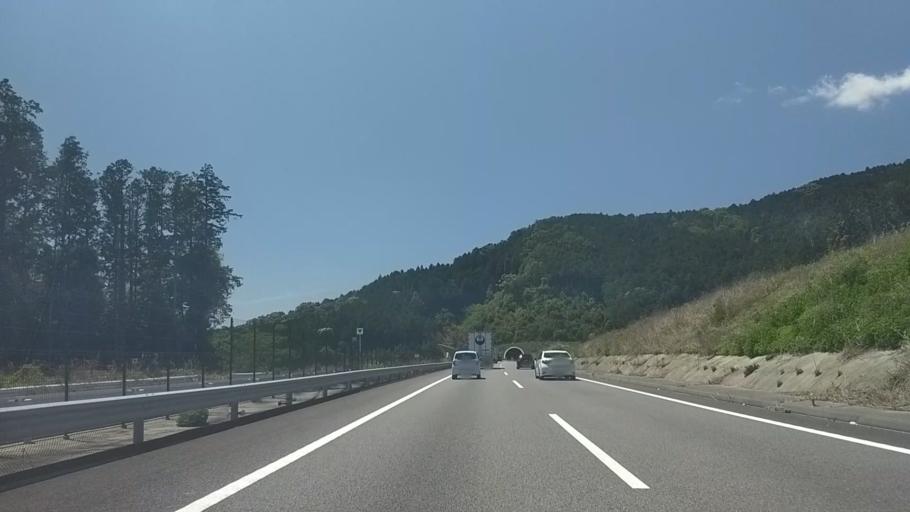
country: JP
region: Aichi
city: Shinshiro
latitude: 34.9191
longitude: 137.4920
